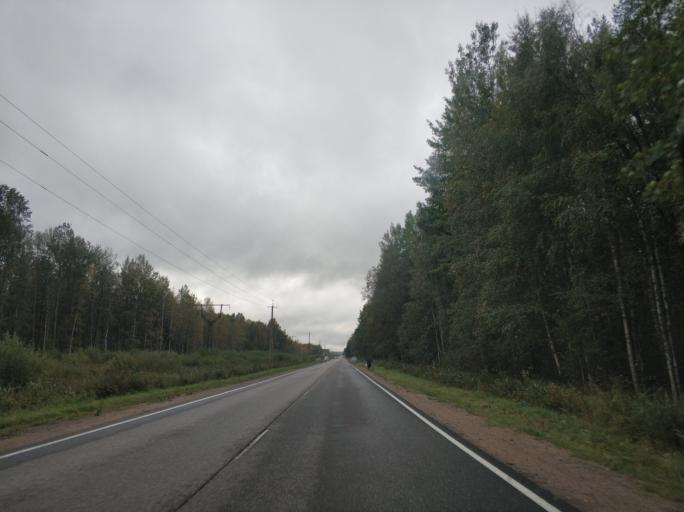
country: RU
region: Leningrad
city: Borisova Griva
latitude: 60.1100
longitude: 30.9610
